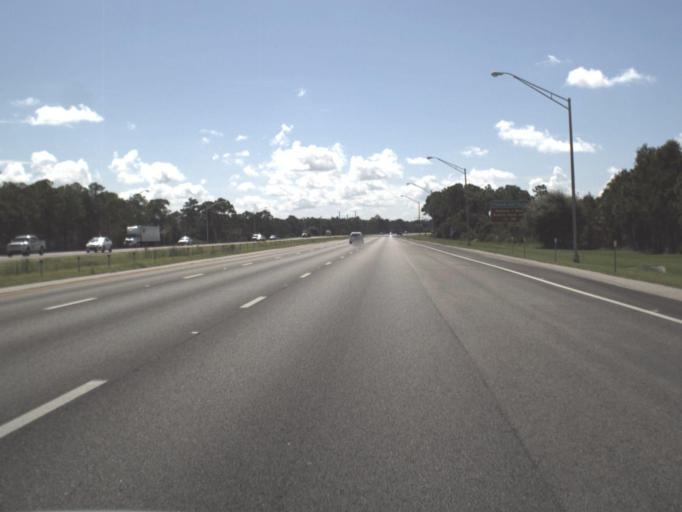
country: US
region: Florida
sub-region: Charlotte County
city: Charlotte Park
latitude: 26.8743
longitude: -81.9801
